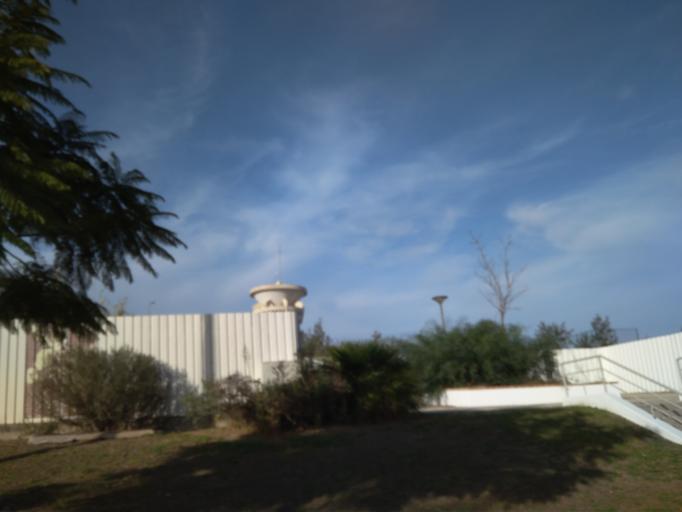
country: PT
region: Faro
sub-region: Faro
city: Faro
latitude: 37.0259
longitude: -7.9342
